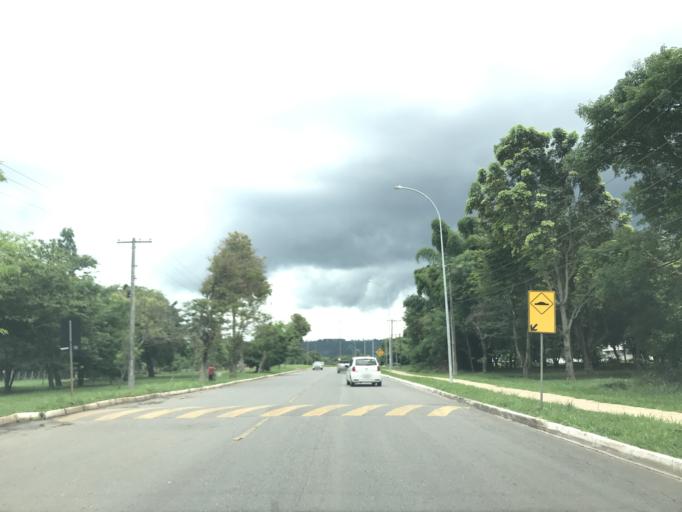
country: BR
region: Federal District
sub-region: Brasilia
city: Brasilia
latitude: -15.6519
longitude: -47.8136
